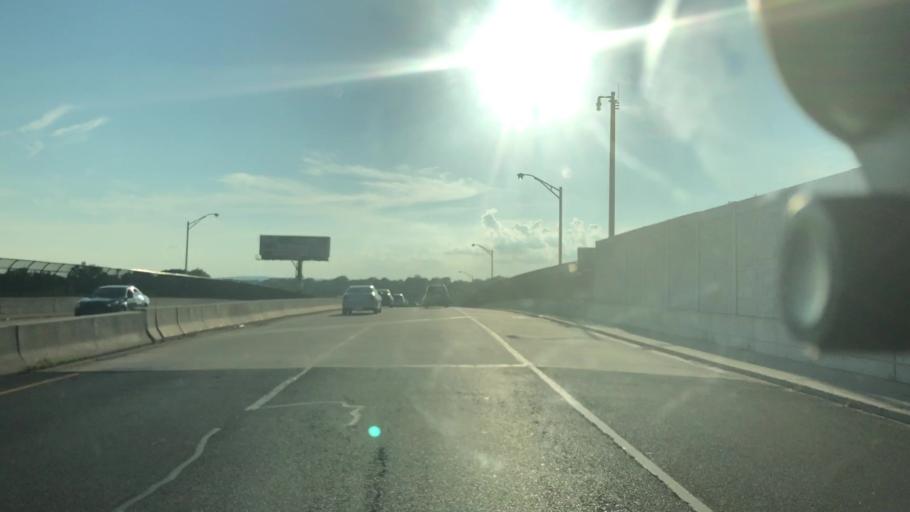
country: US
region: New Jersey
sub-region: Union County
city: Hillside
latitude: 40.6992
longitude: -74.2307
